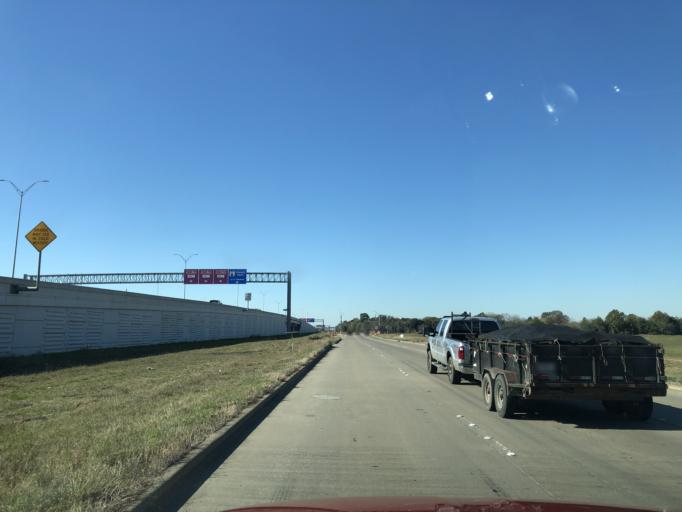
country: US
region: Texas
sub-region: Brazoria County
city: Brookside Village
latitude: 29.5974
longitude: -95.3977
